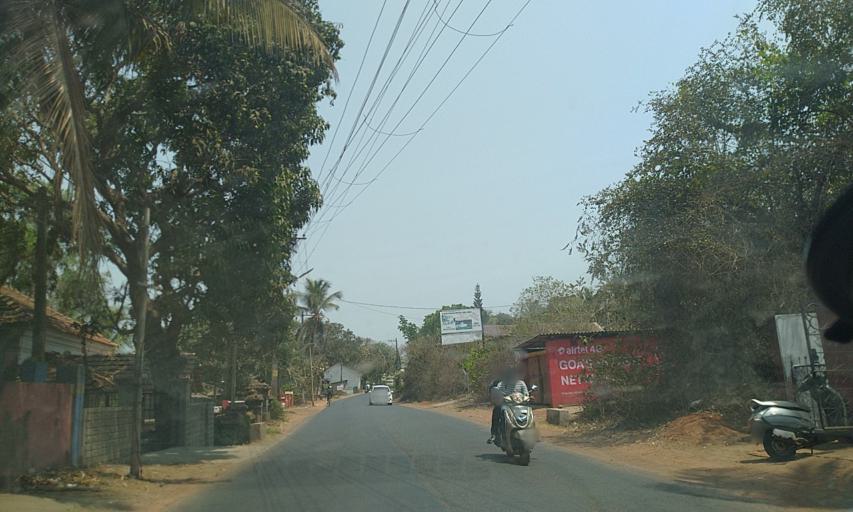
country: IN
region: Goa
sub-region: North Goa
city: Saligao
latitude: 15.5461
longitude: 73.8028
